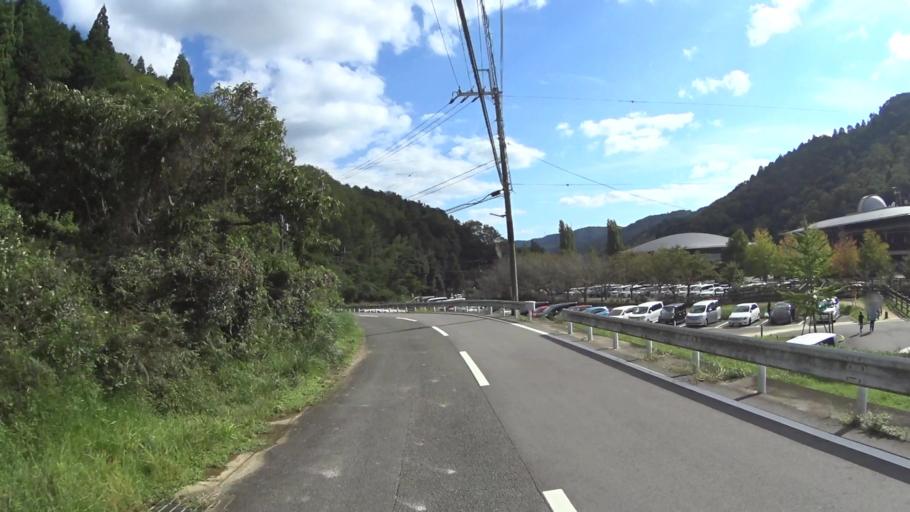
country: JP
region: Shiga Prefecture
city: Otsu-shi
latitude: 34.9352
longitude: 135.8573
